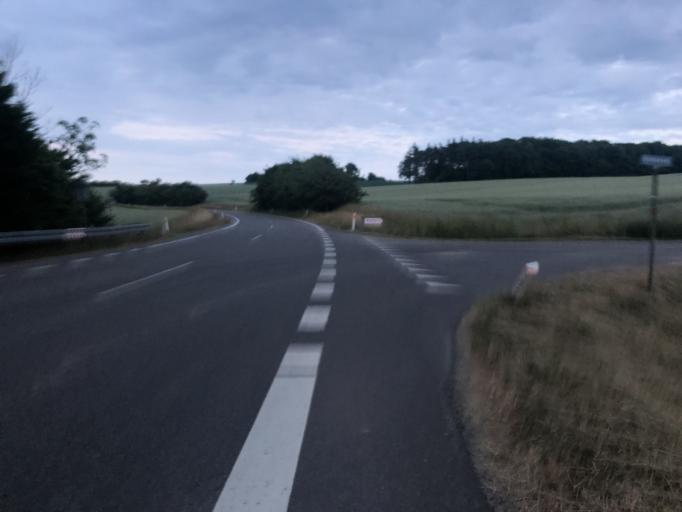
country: DK
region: Capital Region
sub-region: Bornholm Kommune
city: Akirkeby
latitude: 55.2069
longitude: 14.9426
